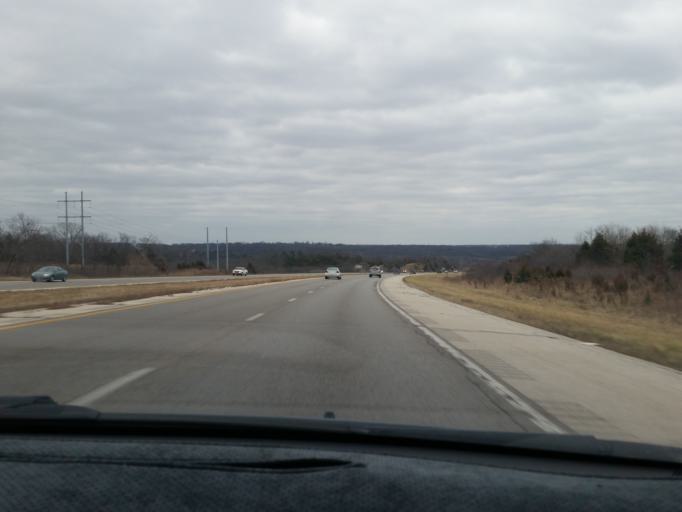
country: US
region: Kansas
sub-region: Johnson County
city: De Soto
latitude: 38.9602
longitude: -94.9352
